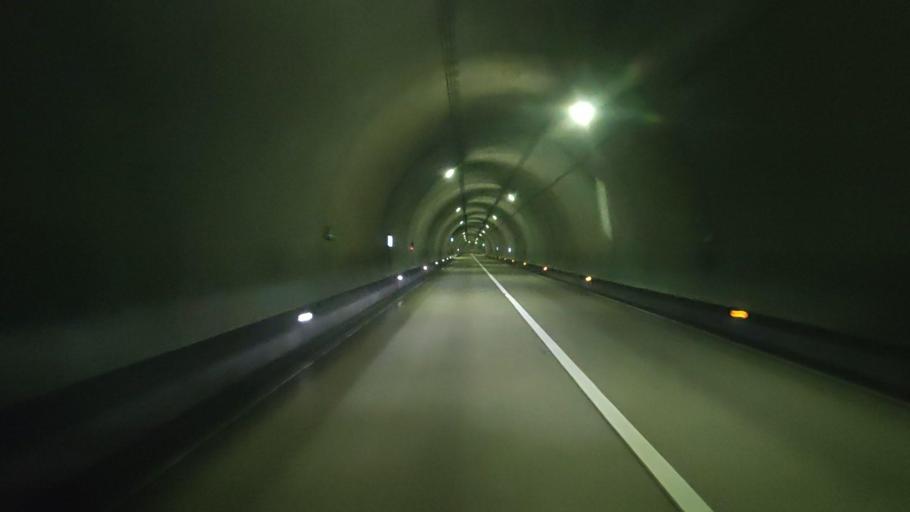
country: JP
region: Wakayama
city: Shingu
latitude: 33.8547
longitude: 135.8536
